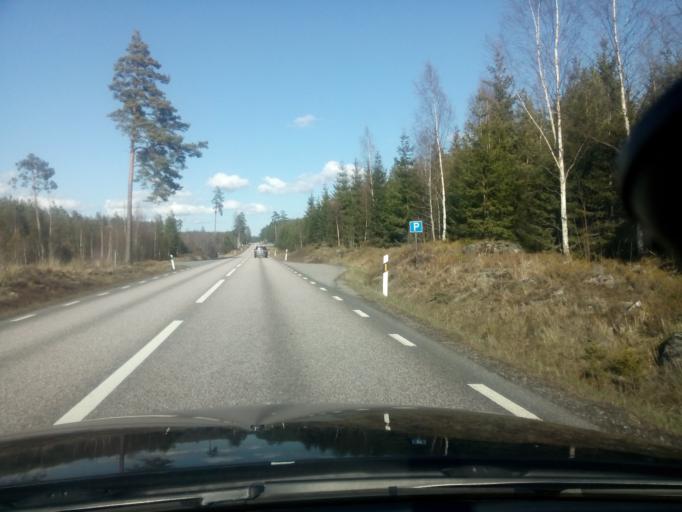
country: SE
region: Soedermanland
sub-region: Strangnas Kommun
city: Akers Styckebruk
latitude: 59.2180
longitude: 16.9026
